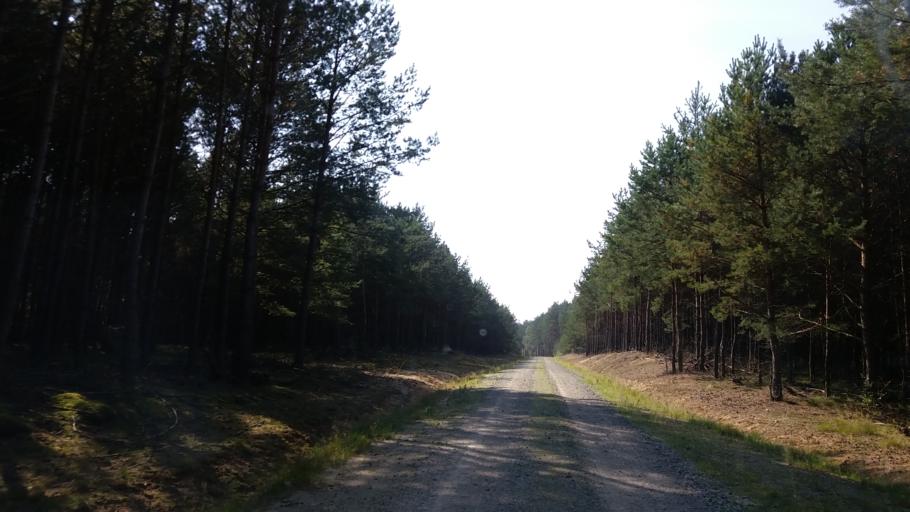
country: PL
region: West Pomeranian Voivodeship
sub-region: Powiat drawski
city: Kalisz Pomorski
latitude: 53.1903
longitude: 15.9605
